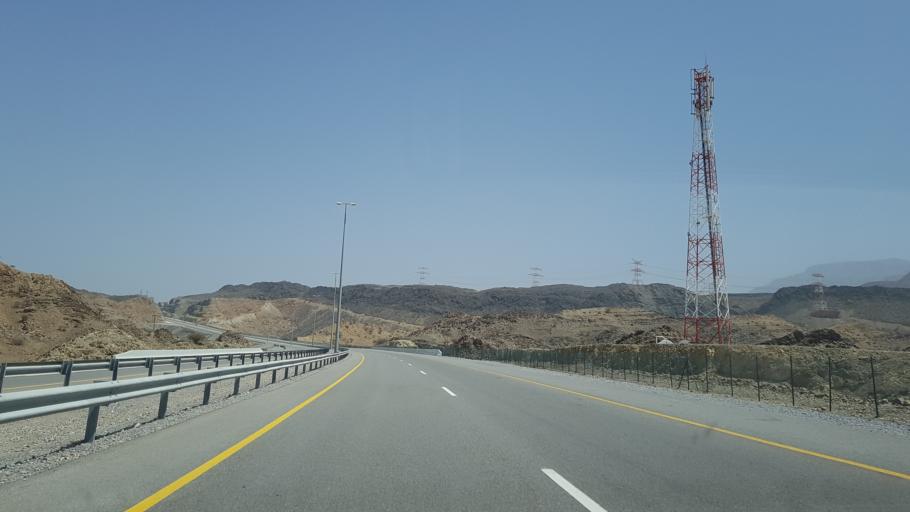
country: OM
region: Muhafazat Masqat
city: Muscat
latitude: 23.2157
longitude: 58.7955
